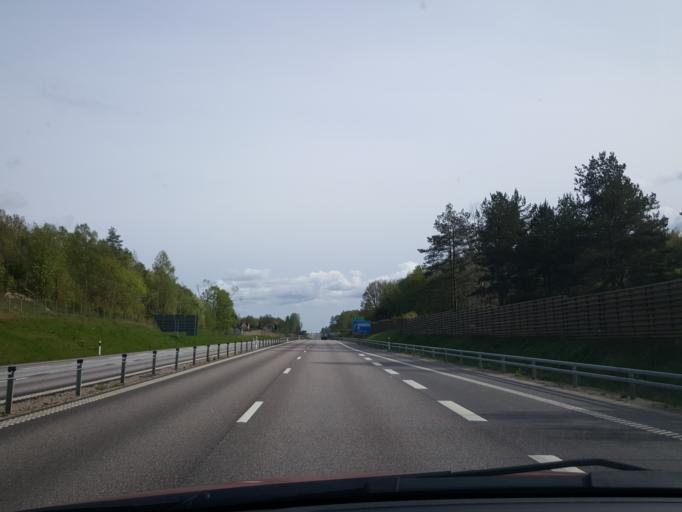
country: SE
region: Vaestra Goetaland
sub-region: Lilla Edets Kommun
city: Lilla Edet
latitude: 58.1398
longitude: 12.1356
